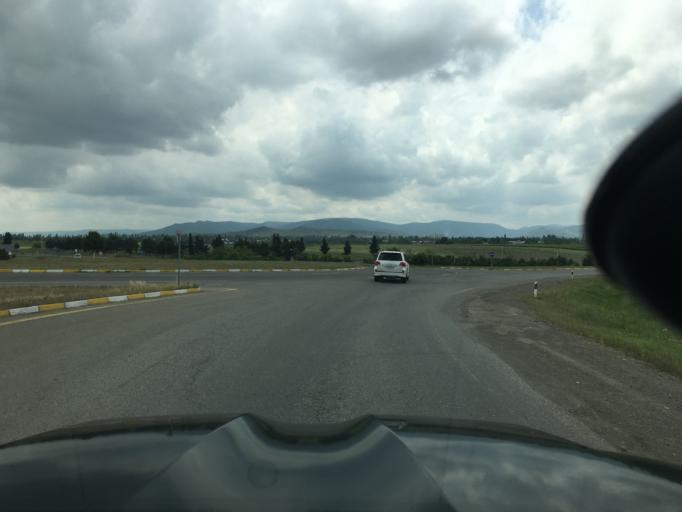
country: AZ
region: Tovuz
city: Tovuz
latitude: 40.9793
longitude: 45.6680
